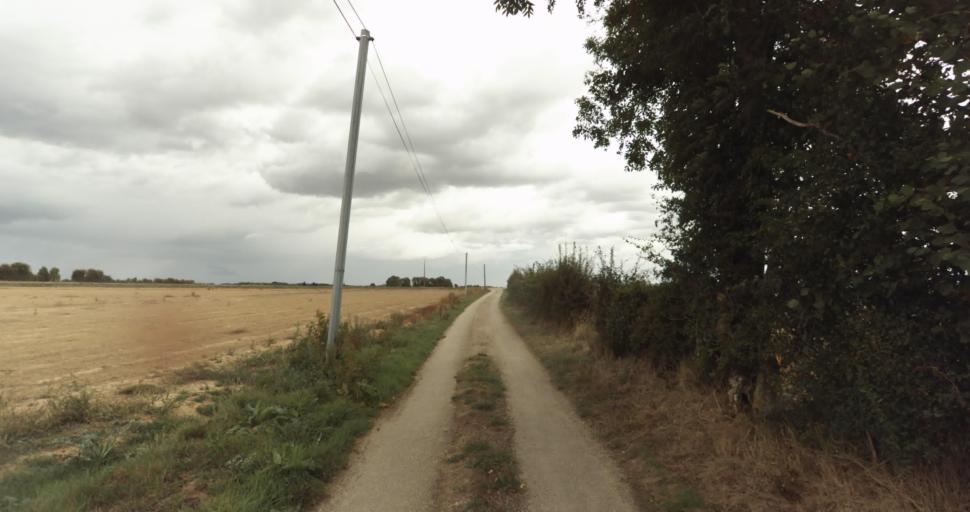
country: FR
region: Lower Normandy
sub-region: Departement du Calvados
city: Orbec
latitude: 48.9134
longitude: 0.3714
